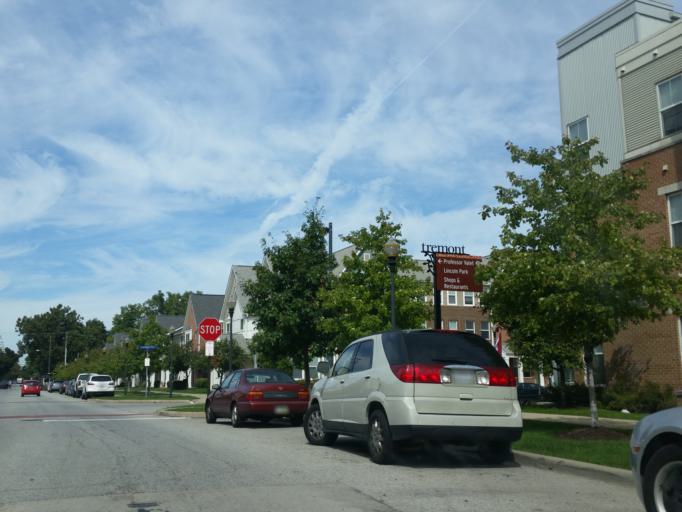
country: US
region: Ohio
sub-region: Cuyahoga County
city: Cleveland
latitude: 41.4776
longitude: -81.6801
